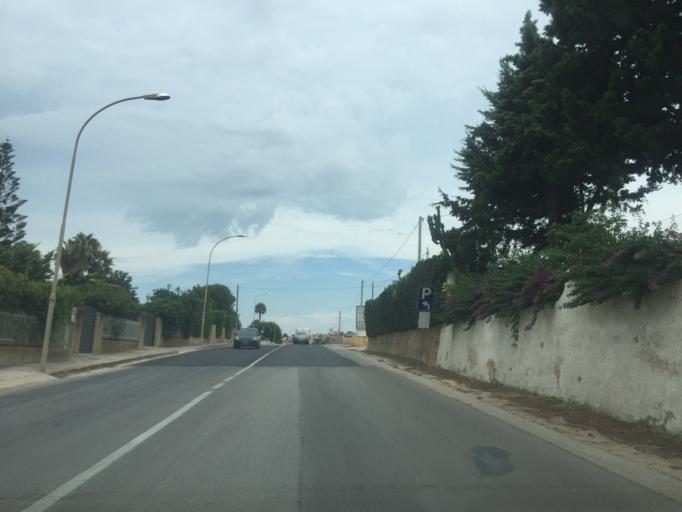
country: IT
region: Sicily
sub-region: Ragusa
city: Marina di Ragusa
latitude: 36.7849
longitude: 14.5638
